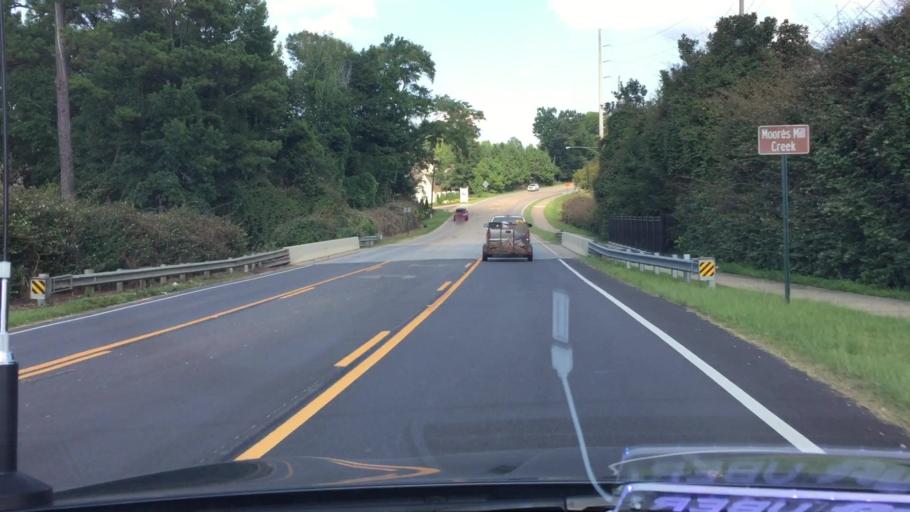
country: US
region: Alabama
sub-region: Lee County
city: Auburn
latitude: 32.5860
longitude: -85.4500
